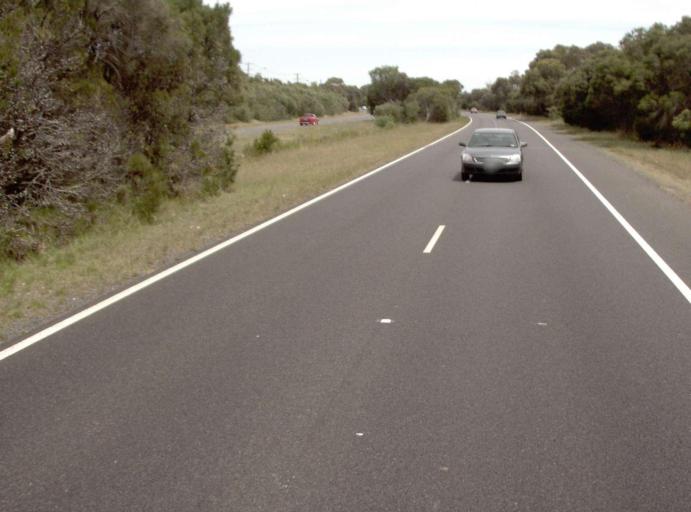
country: AU
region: Victoria
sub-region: Mornington Peninsula
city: McCrae
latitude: -38.3579
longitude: 144.9238
